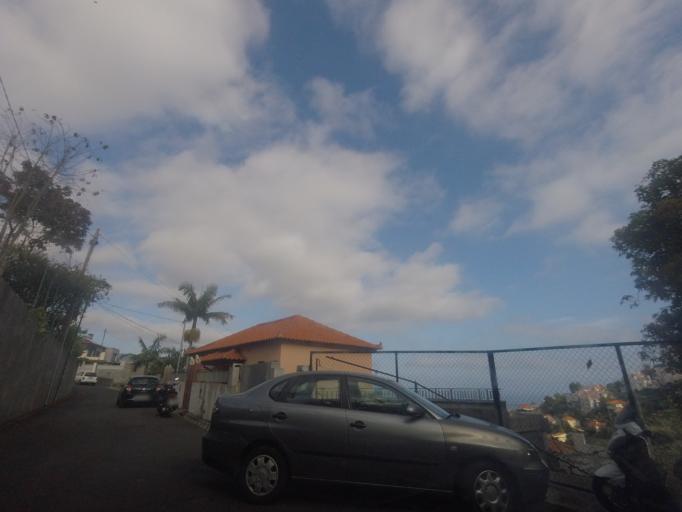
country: PT
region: Madeira
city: Camara de Lobos
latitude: 32.6625
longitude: -16.9402
